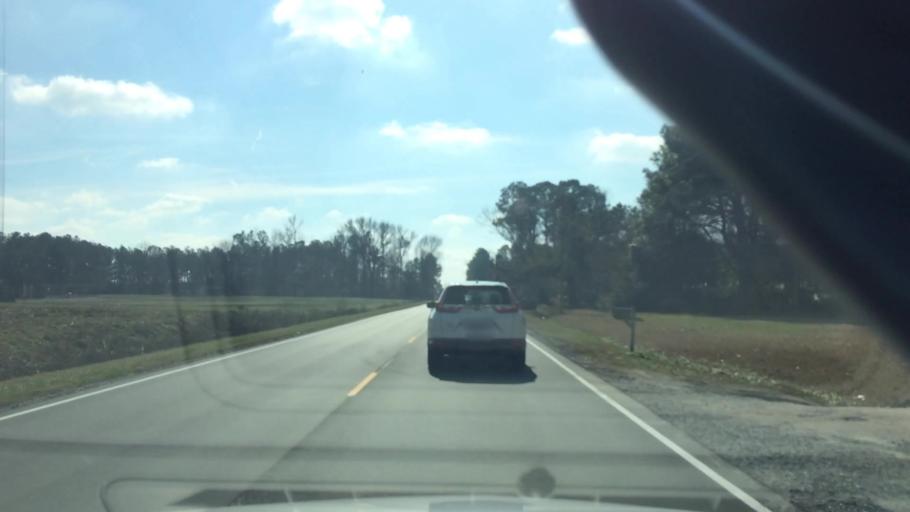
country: US
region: North Carolina
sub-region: Duplin County
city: Beulaville
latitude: 34.9363
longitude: -77.7705
